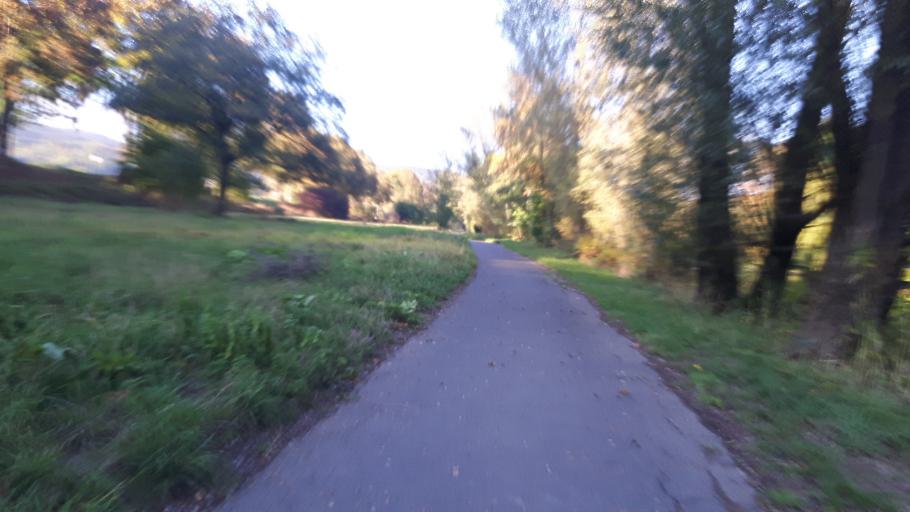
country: DE
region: Rheinland-Pfalz
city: Werkhausen
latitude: 50.8007
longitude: 7.5382
